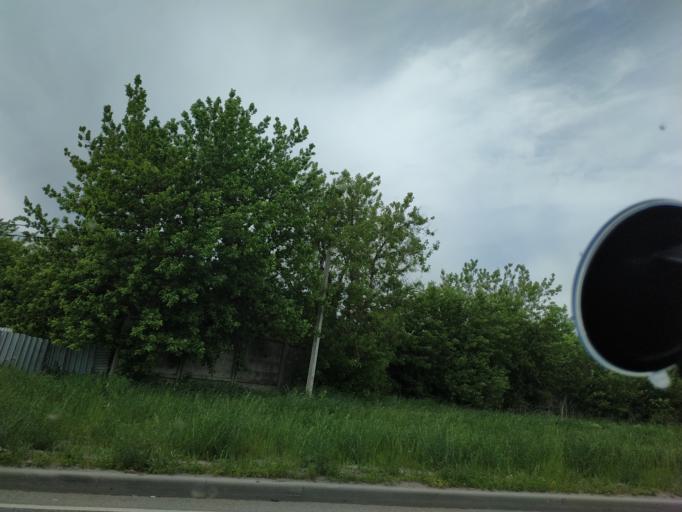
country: RU
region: Moskovskaya
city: Zhukovskiy
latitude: 55.5703
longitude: 38.1149
